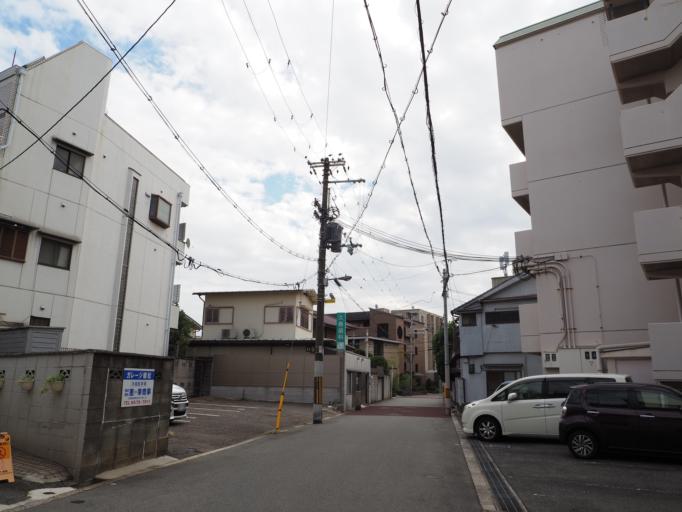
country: JP
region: Osaka
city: Sakai
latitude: 34.6232
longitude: 135.5027
